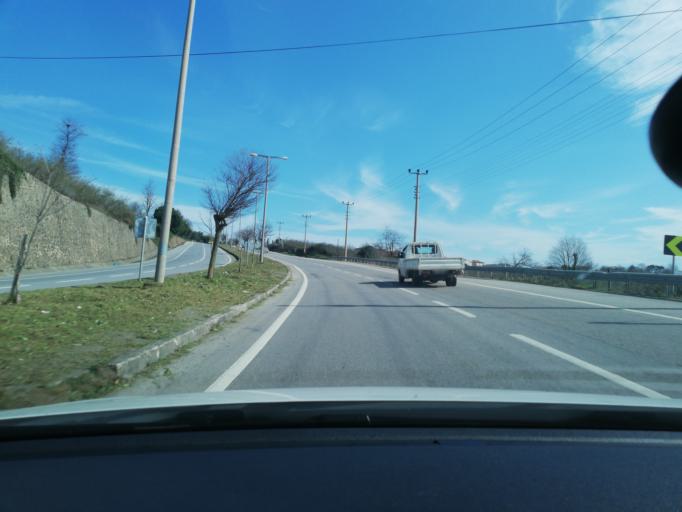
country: TR
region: Duzce
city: Akcakoca
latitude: 41.0833
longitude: 31.1608
